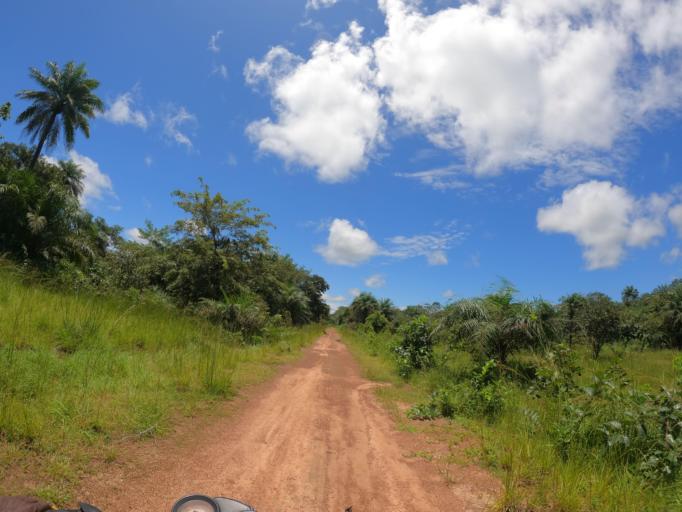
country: SL
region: Northern Province
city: Makeni
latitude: 9.0864
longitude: -12.2666
